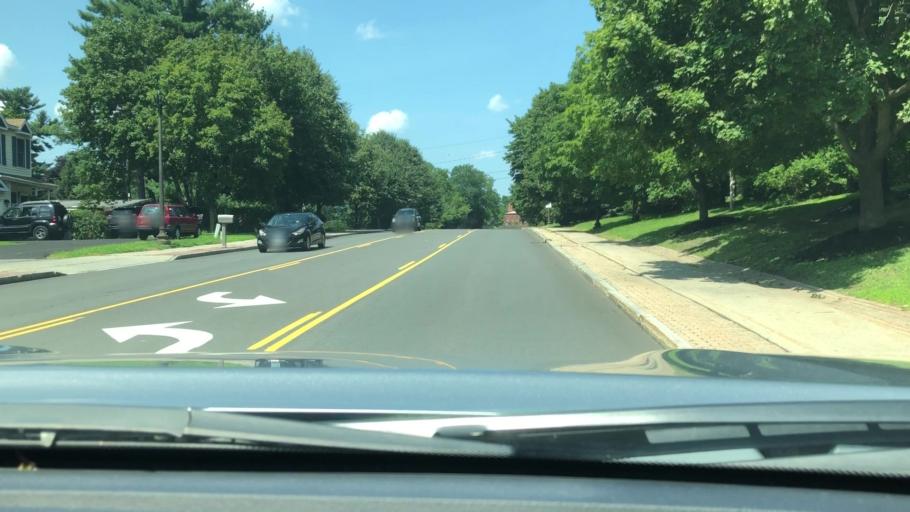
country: US
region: New York
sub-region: Dutchess County
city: Beacon
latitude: 41.5033
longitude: -73.9813
